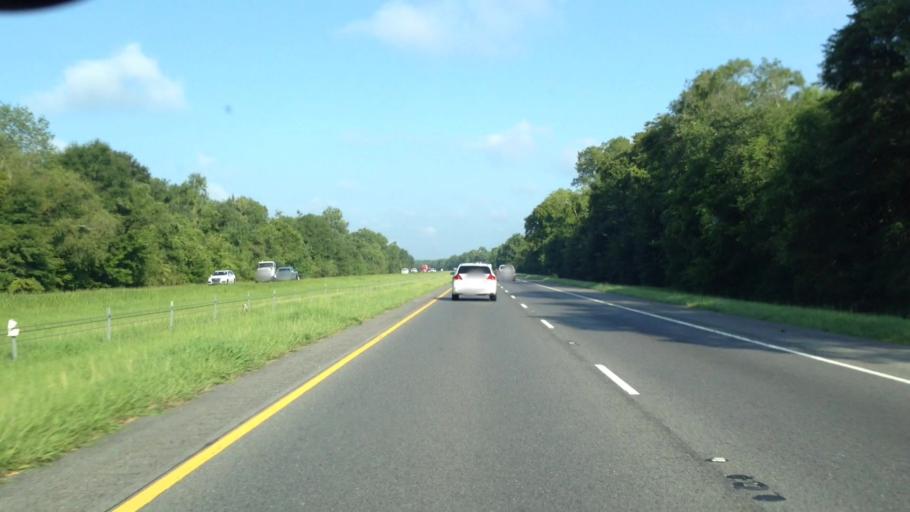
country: US
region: Louisiana
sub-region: Saint James Parish
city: Grand Point
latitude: 30.1464
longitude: -90.7682
